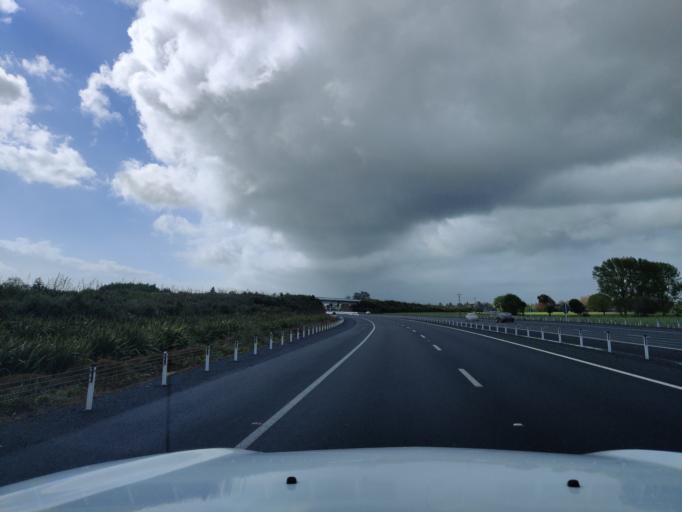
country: NZ
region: Waikato
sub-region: Waipa District
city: Cambridge
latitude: -37.8650
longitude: 175.4028
